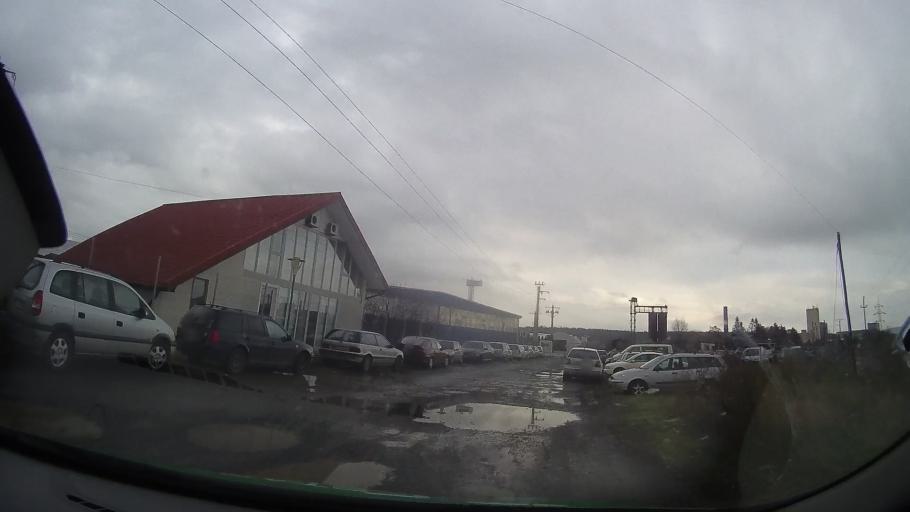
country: RO
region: Mures
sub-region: Municipiul Reghin
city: Iernuteni
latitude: 46.7731
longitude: 24.7205
